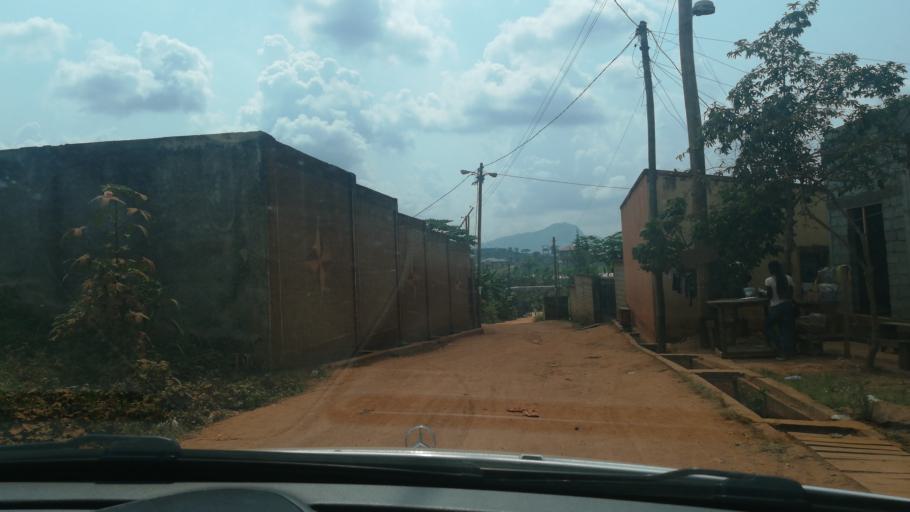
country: CM
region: Centre
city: Yaounde
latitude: 3.7852
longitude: 11.4893
